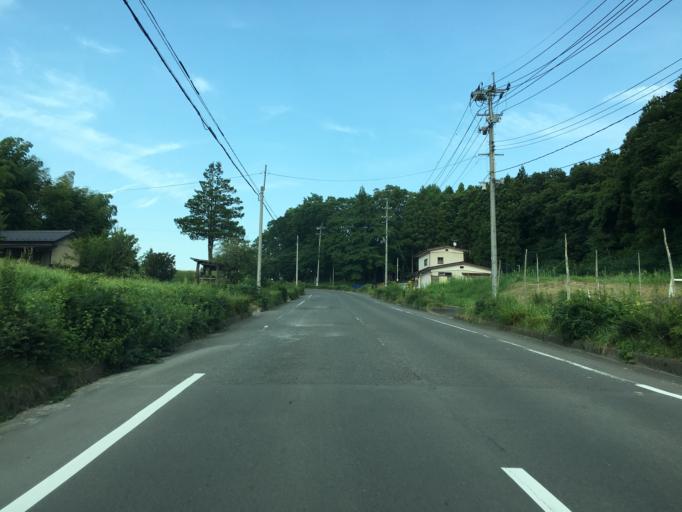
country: JP
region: Fukushima
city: Nihommatsu
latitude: 37.5812
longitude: 140.4364
